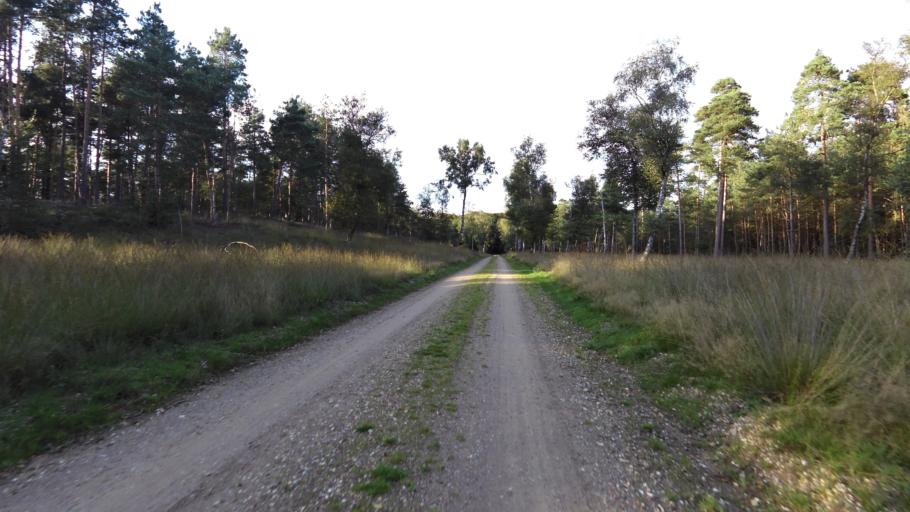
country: NL
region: Gelderland
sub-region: Gemeente Apeldoorn
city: Uddel
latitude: 52.2901
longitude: 5.8679
